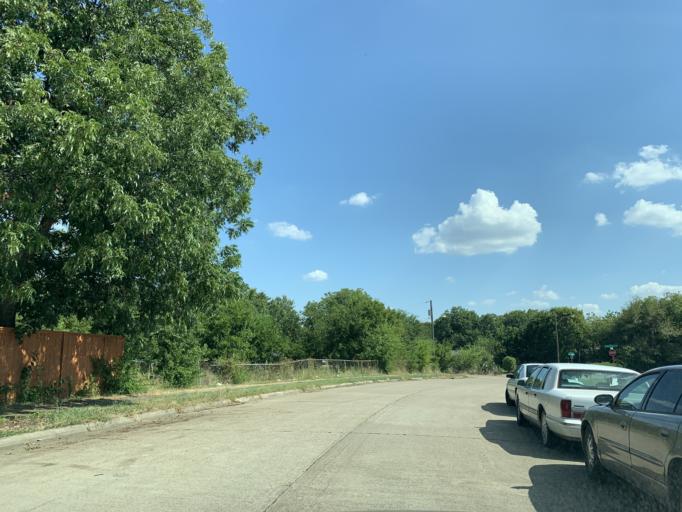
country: US
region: Texas
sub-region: Dallas County
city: Hutchins
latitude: 32.6559
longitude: -96.7726
